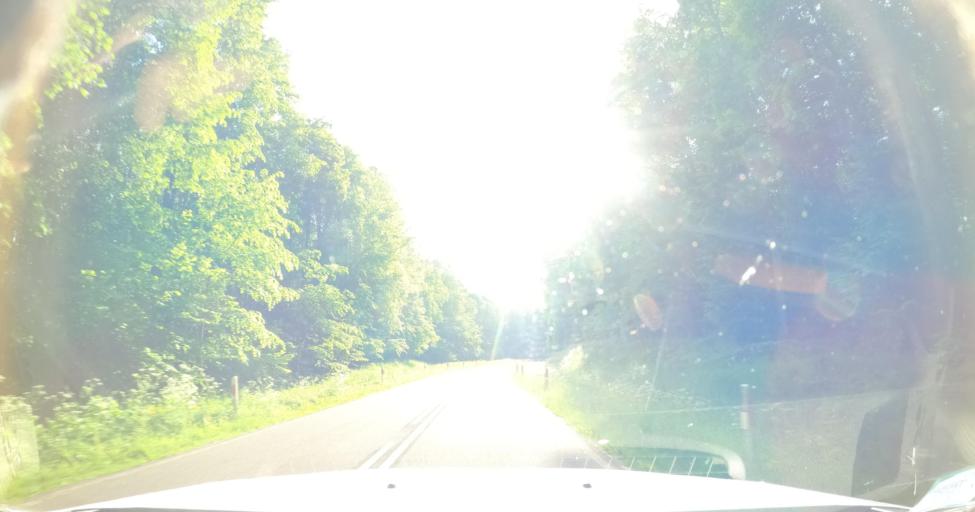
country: PL
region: Warmian-Masurian Voivodeship
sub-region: Powiat elblaski
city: Paslek
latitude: 54.0791
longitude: 19.7274
